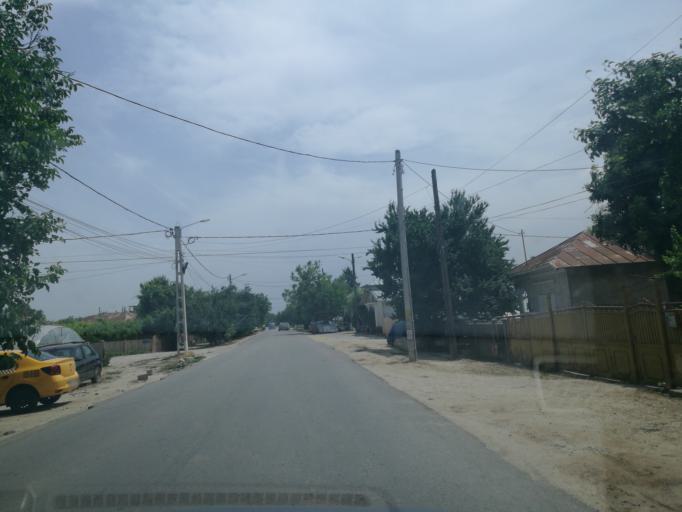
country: RO
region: Ilfov
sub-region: Comuna Vidra
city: Cretesti
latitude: 44.2756
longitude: 26.1368
